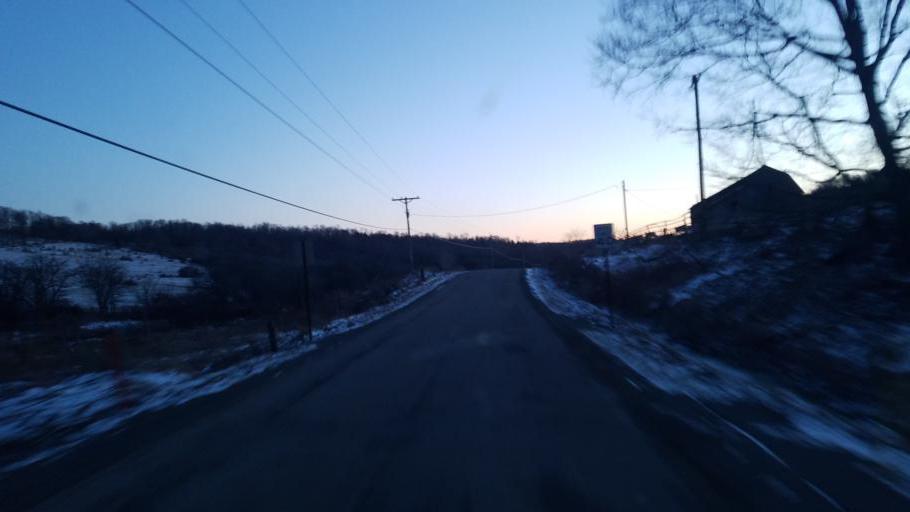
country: US
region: New York
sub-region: Allegany County
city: Andover
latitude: 41.9645
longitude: -77.7617
